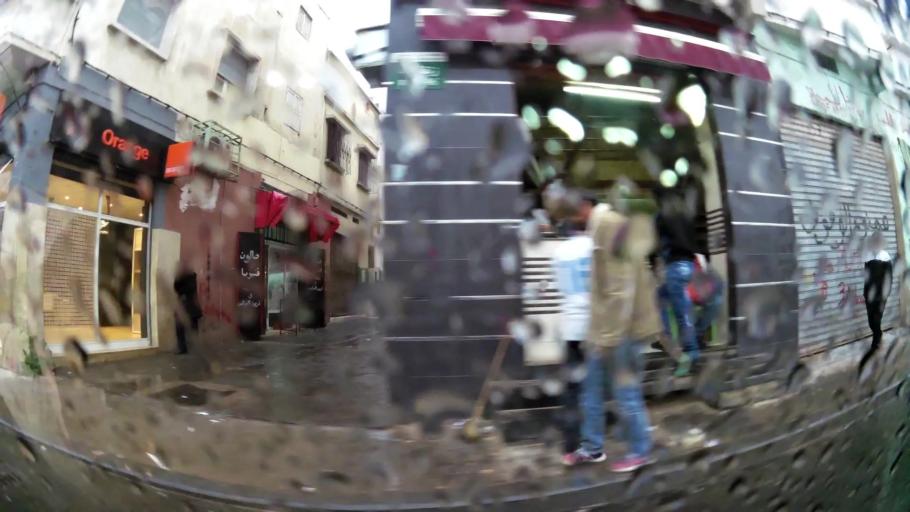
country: MA
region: Grand Casablanca
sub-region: Casablanca
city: Casablanca
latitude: 33.5699
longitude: -7.6034
